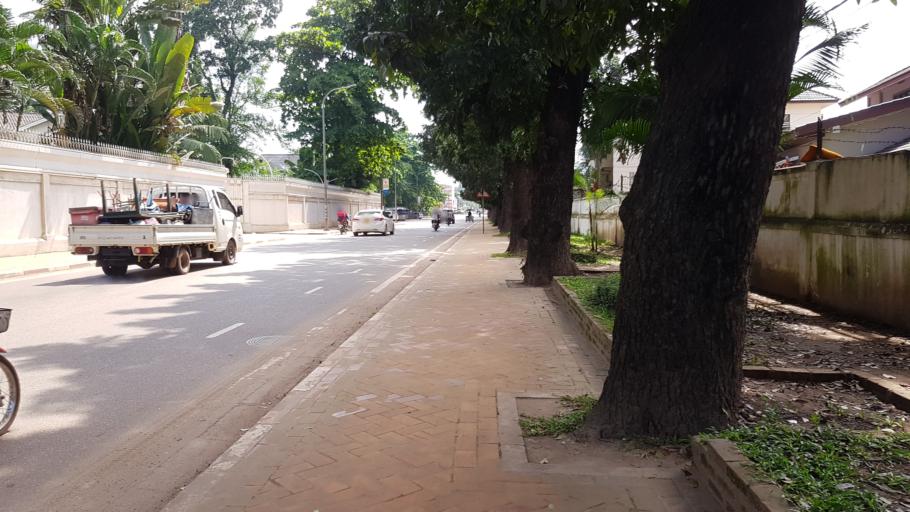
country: LA
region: Vientiane
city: Vientiane
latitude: 17.9612
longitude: 102.6126
